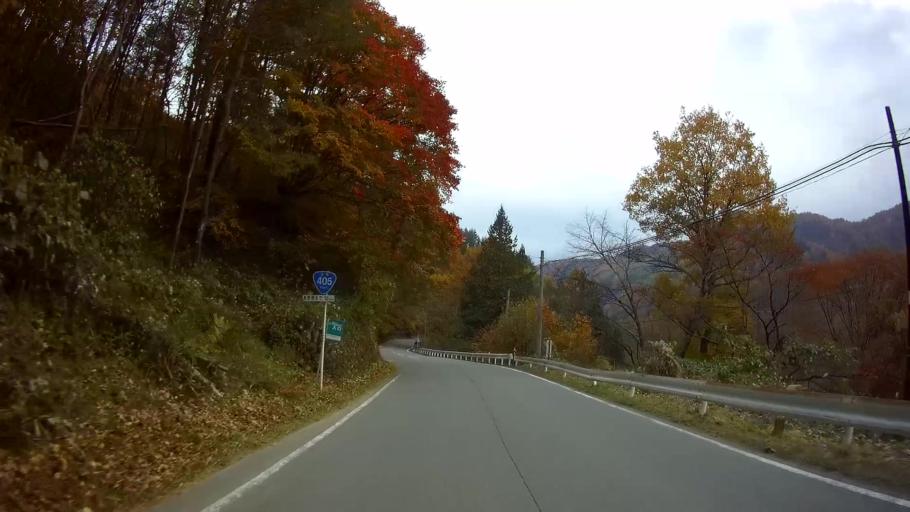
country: JP
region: Gunma
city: Nakanojomachi
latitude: 36.6488
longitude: 138.6506
